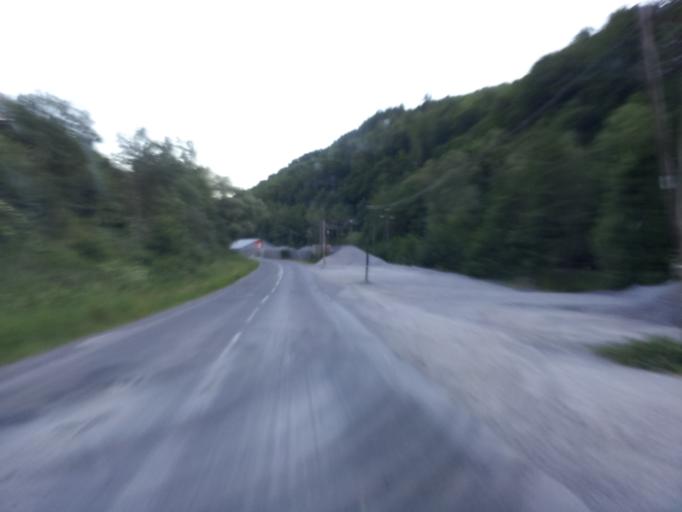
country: SK
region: Banskobystricky
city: Krupina
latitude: 48.3253
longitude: 18.9774
